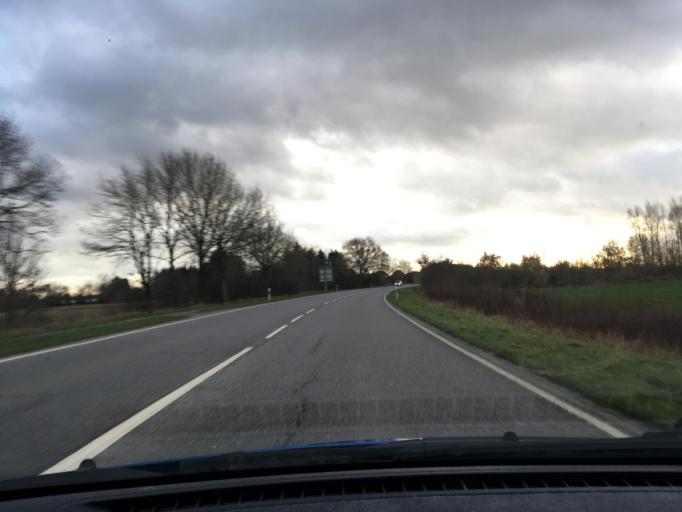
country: DE
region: Schleswig-Holstein
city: Ottenbuttel
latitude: 53.9823
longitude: 9.5003
